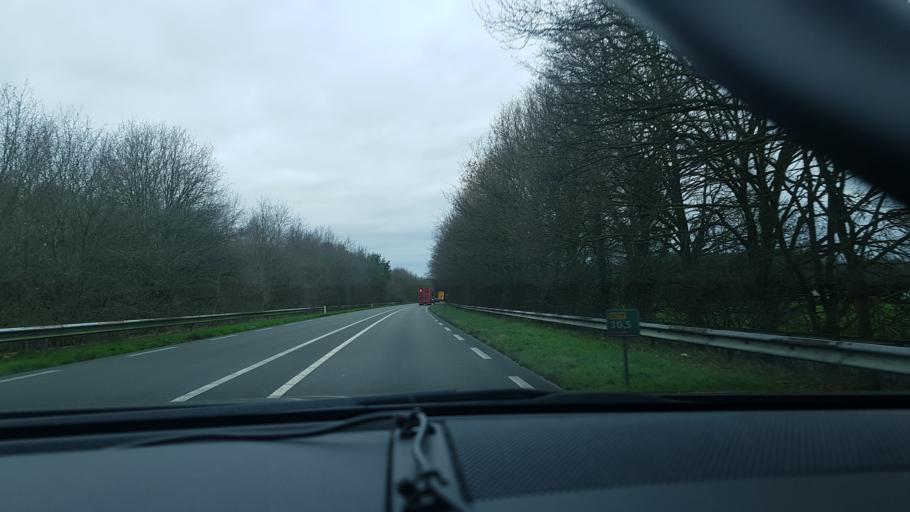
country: NL
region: North Brabant
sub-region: Gemeente Asten
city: Asten
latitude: 51.4288
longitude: 5.7458
